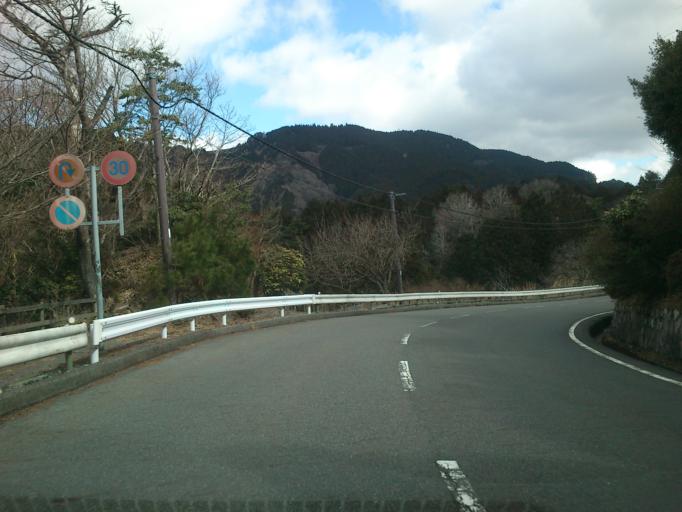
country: JP
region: Shiga Prefecture
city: Otsu-shi
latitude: 35.0533
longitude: 135.8318
